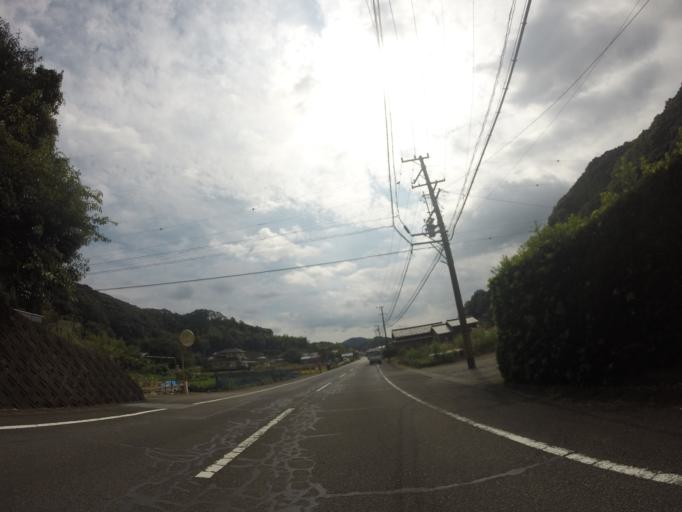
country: JP
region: Shizuoka
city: Shimada
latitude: 34.8710
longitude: 138.1813
